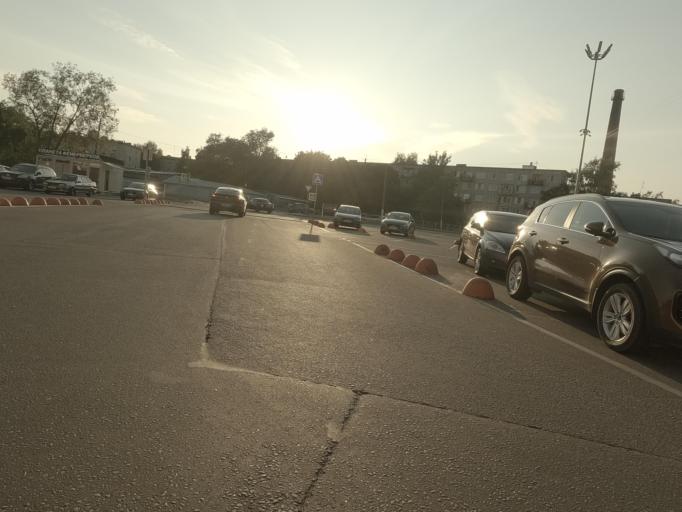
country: RU
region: Leningrad
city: Vyborg
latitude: 60.7078
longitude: 28.7723
